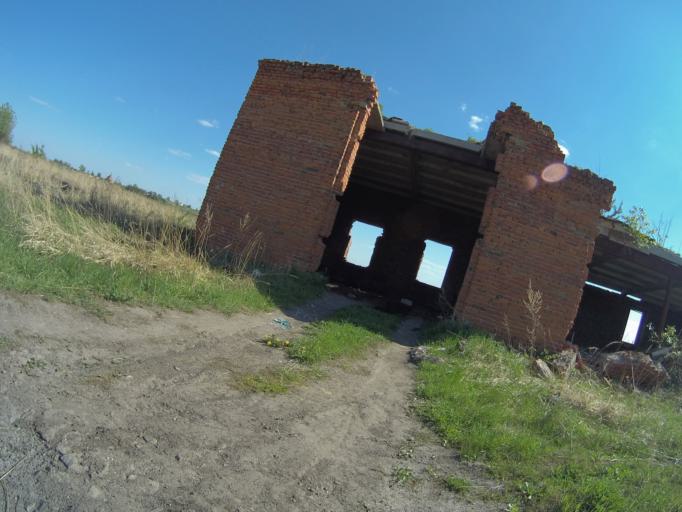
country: RU
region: Vladimir
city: Kideksha
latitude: 56.4169
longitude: 40.4869
